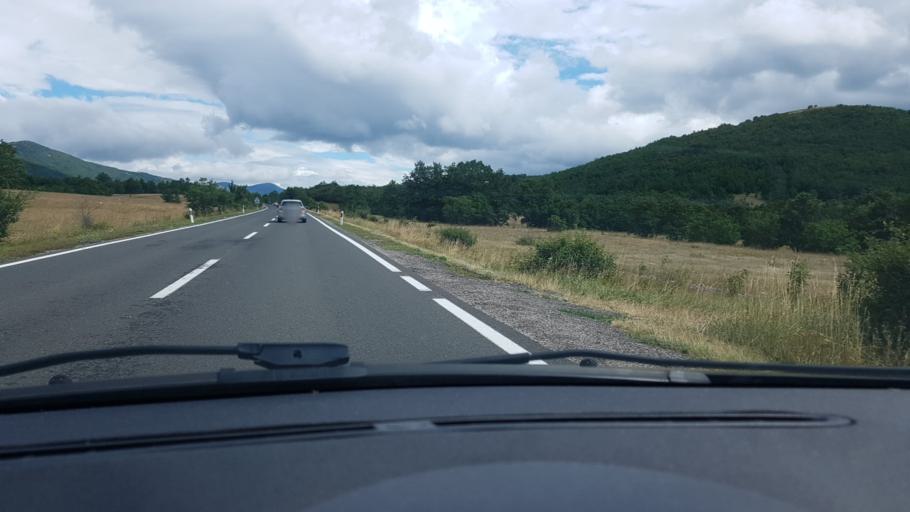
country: HR
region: Zadarska
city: Gracac
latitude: 44.4609
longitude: 15.8100
